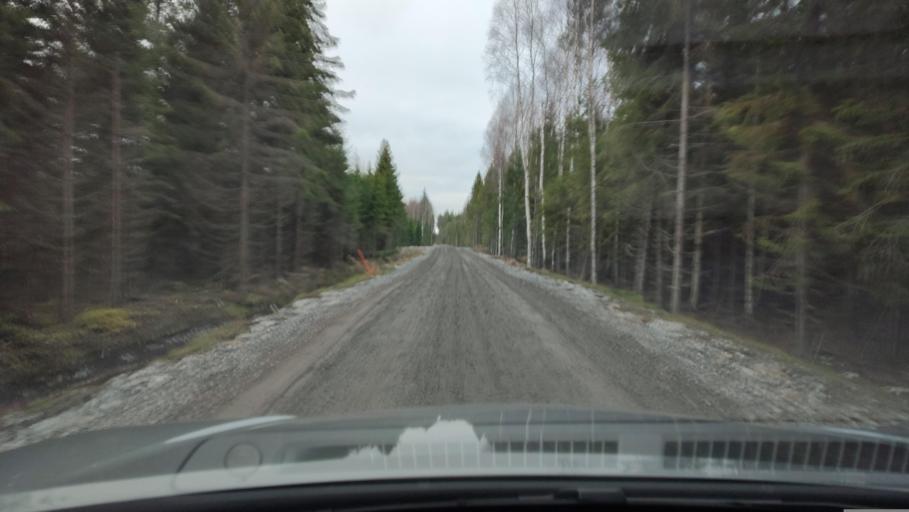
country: FI
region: Ostrobothnia
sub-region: Sydosterbotten
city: Kristinestad
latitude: 62.1901
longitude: 21.5353
